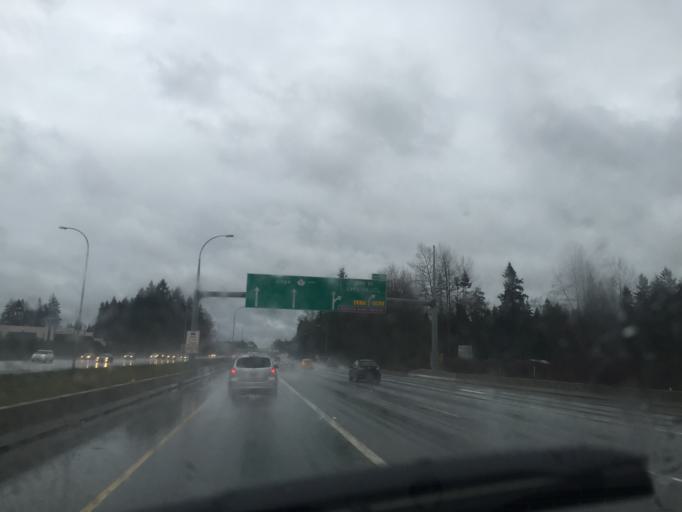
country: CA
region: British Columbia
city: Walnut Grove
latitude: 49.1672
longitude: -122.6807
